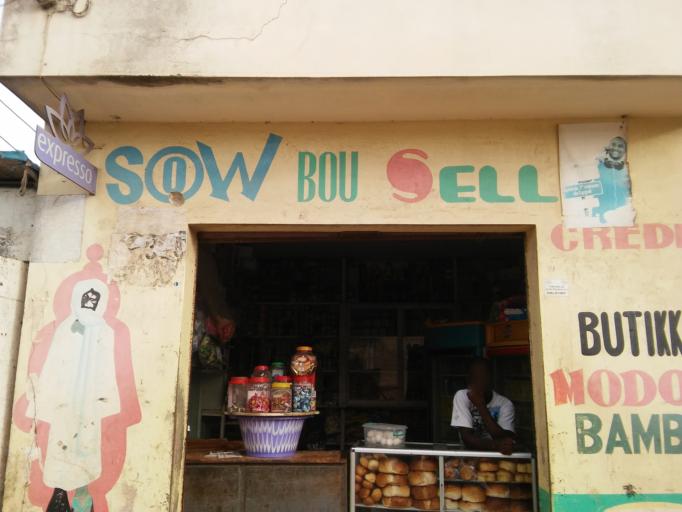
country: SN
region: Dakar
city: Pikine
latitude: 14.7431
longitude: -17.4200
